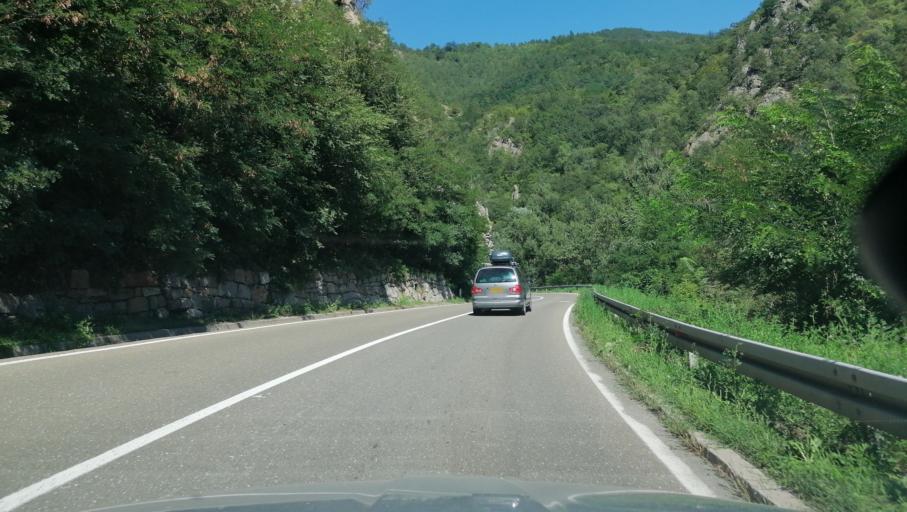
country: RS
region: Central Serbia
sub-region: Raski Okrug
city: Raska
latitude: 43.5030
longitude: 20.6157
